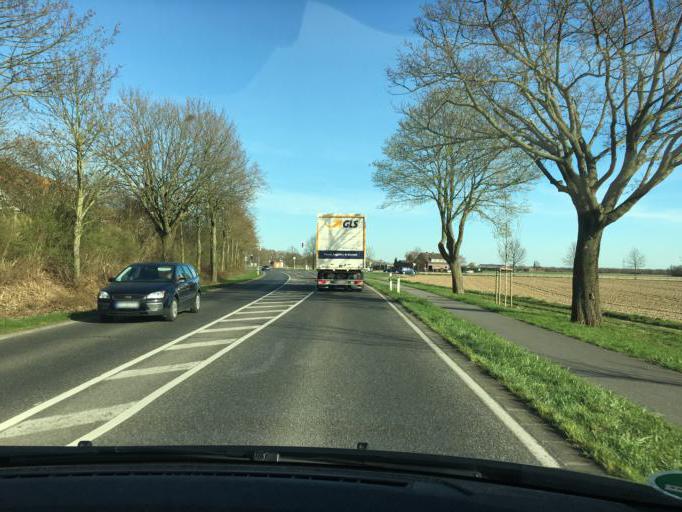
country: DE
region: North Rhine-Westphalia
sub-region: Regierungsbezirk Dusseldorf
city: Kaarst
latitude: 51.1915
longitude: 6.6043
